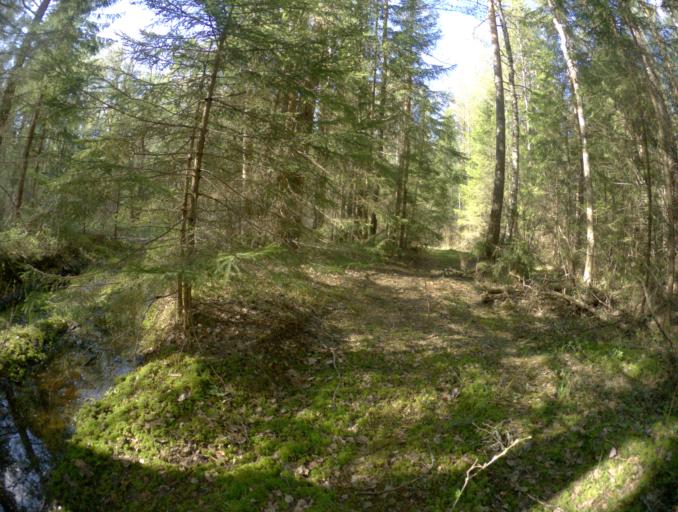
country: RU
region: Vladimir
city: Golovino
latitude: 55.9176
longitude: 40.4405
